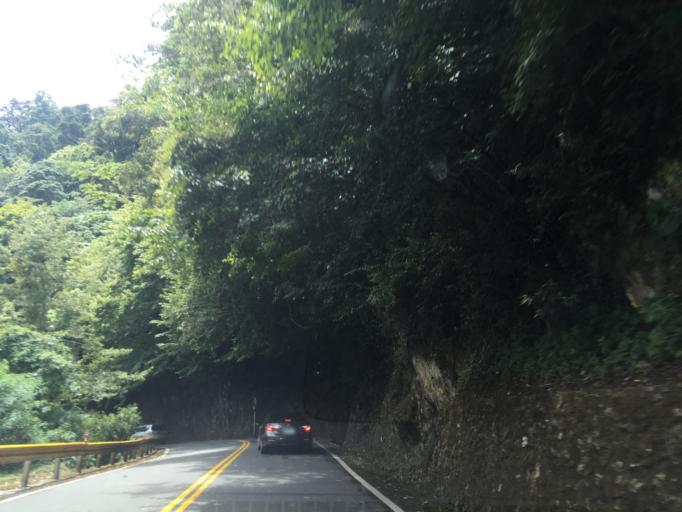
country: TW
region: Taiwan
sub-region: Hualien
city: Hualian
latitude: 24.1809
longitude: 121.3923
